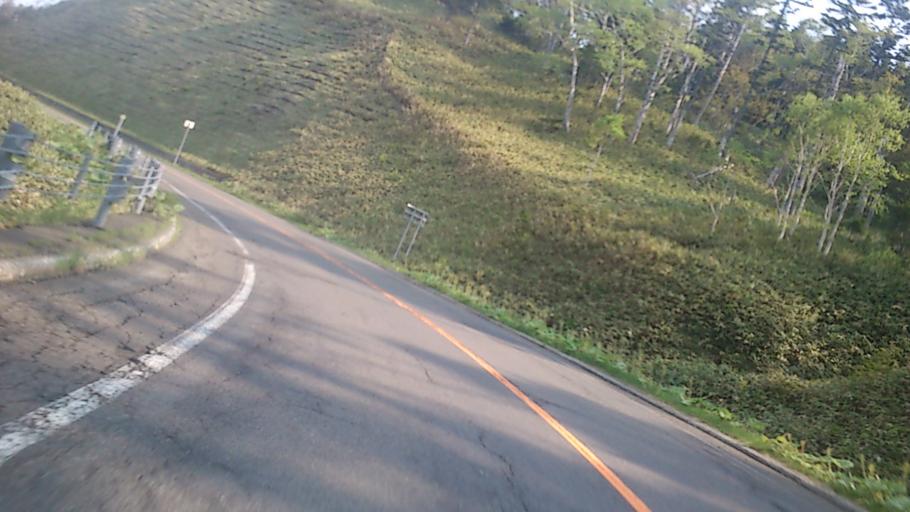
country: JP
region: Hokkaido
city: Bihoro
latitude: 43.4508
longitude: 144.2278
